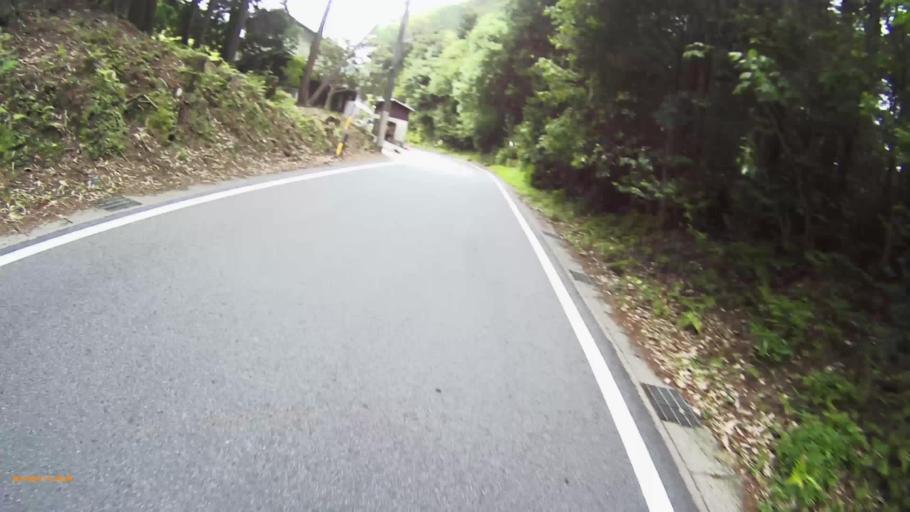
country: JP
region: Gifu
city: Nakatsugawa
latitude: 35.4663
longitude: 137.4329
